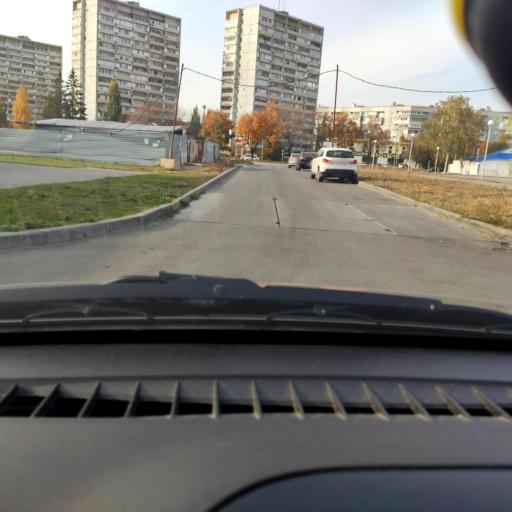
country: RU
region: Samara
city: Tol'yatti
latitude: 53.5307
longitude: 49.3435
